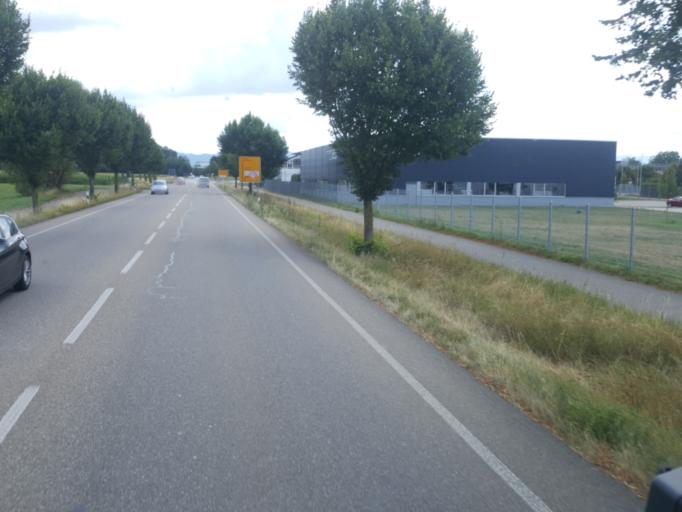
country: DE
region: Baden-Wuerttemberg
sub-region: Freiburg Region
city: Teningen
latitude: 48.1346
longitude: 7.8150
